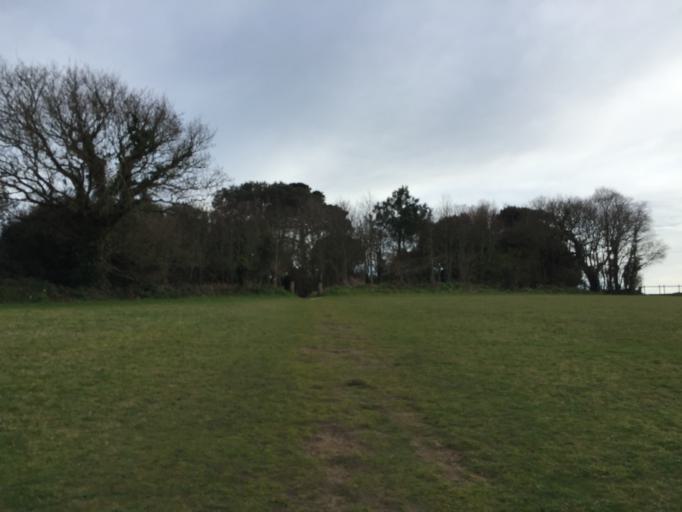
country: JE
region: St Helier
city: Saint Helier
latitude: 49.1871
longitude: -2.2151
